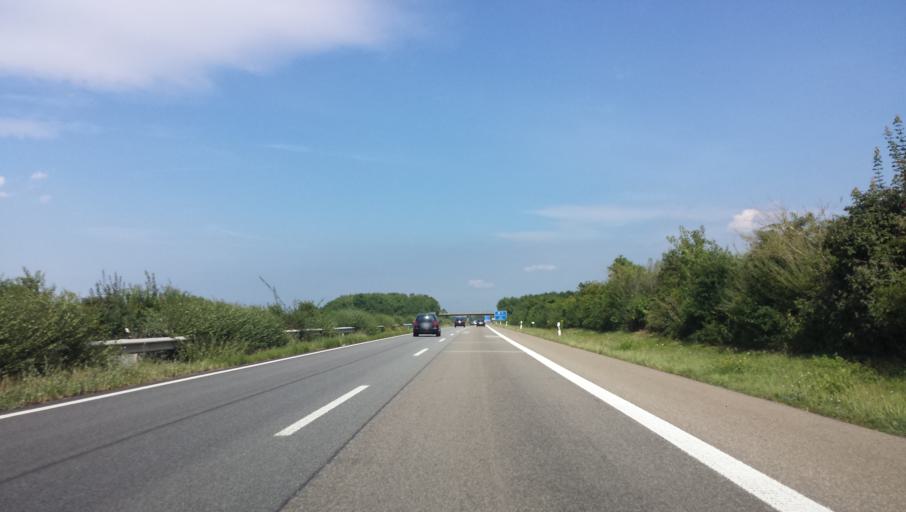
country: DE
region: Rheinland-Pfalz
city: Kirrweiler
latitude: 49.3155
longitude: 8.1646
